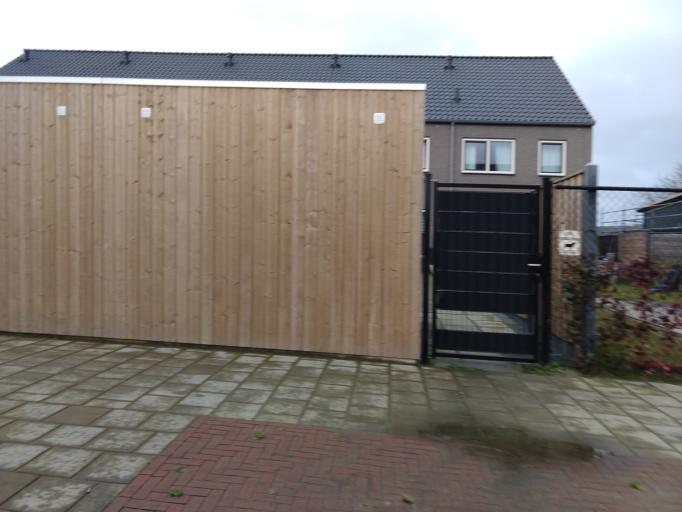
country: NL
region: Zeeland
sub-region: Gemeente Goes
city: Goes
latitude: 51.5007
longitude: 3.8801
